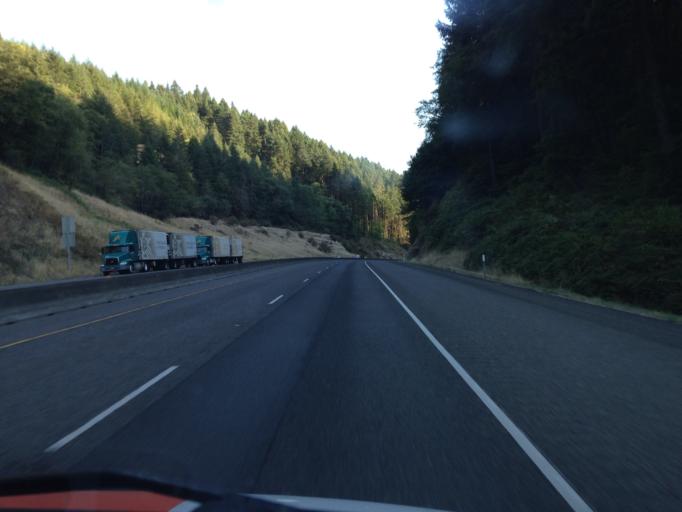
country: US
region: Oregon
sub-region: Douglas County
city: Drain
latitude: 43.6932
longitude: -123.2004
